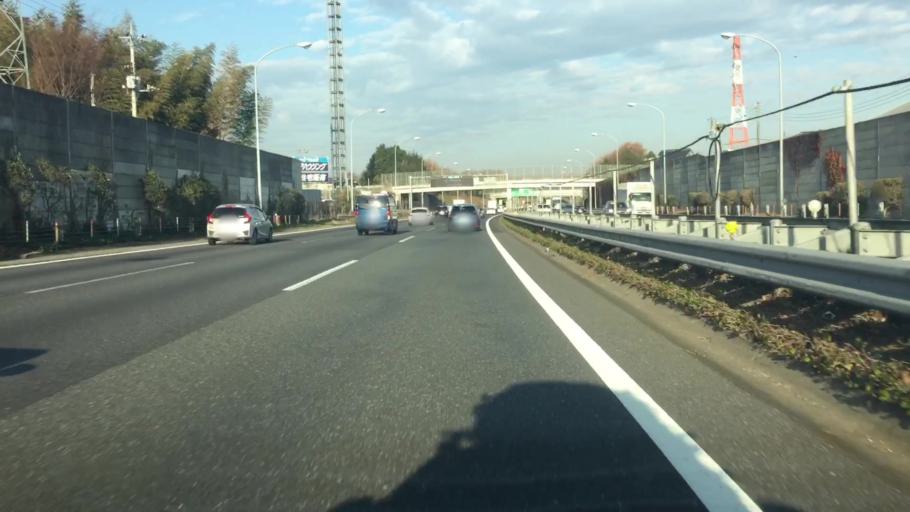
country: JP
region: Saitama
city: Sakado
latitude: 35.9196
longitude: 139.4170
